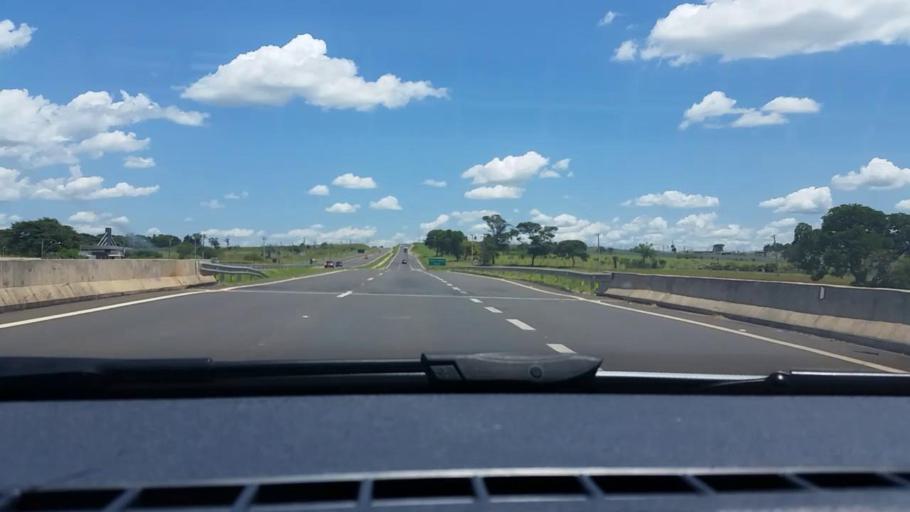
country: BR
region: Sao Paulo
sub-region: Bauru
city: Bauru
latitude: -22.3857
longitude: -49.0716
